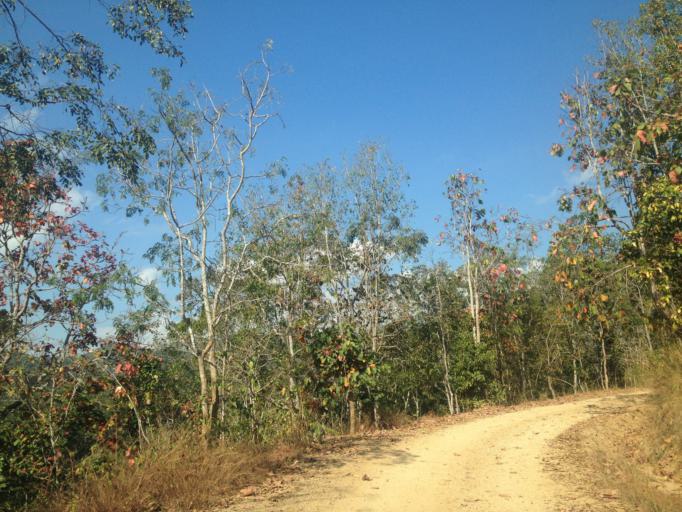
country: TH
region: Mae Hong Son
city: Ban Huai I Huak
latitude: 18.1299
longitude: 98.1949
